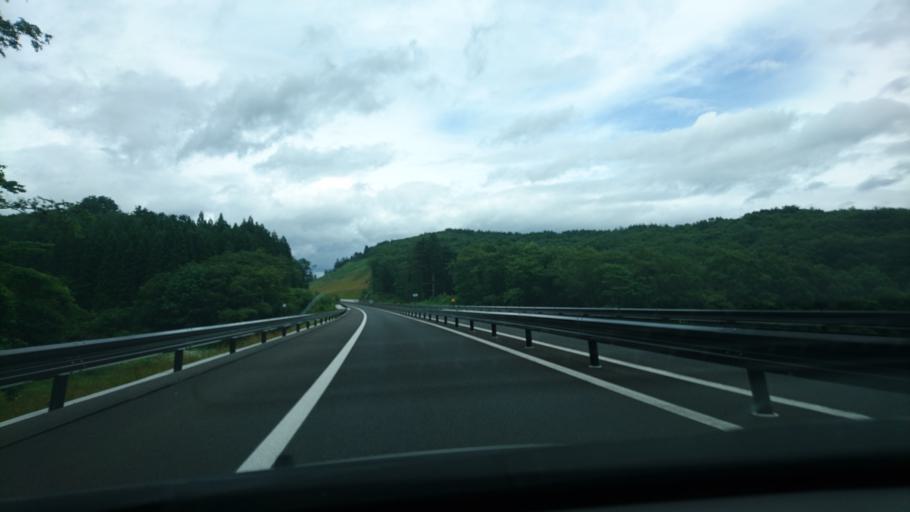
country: JP
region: Iwate
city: Yamada
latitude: 39.5458
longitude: 141.9243
